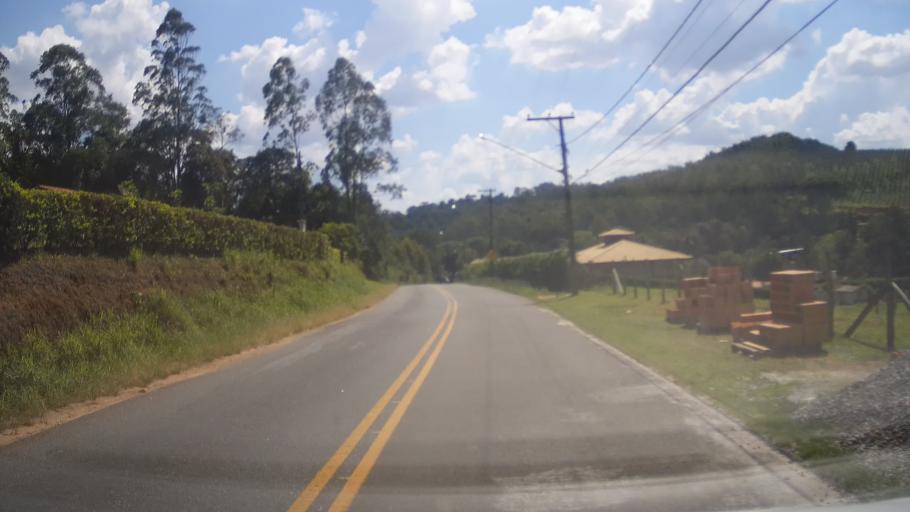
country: BR
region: Sao Paulo
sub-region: Varzea Paulista
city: Varzea Paulista
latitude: -23.1314
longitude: -46.8259
